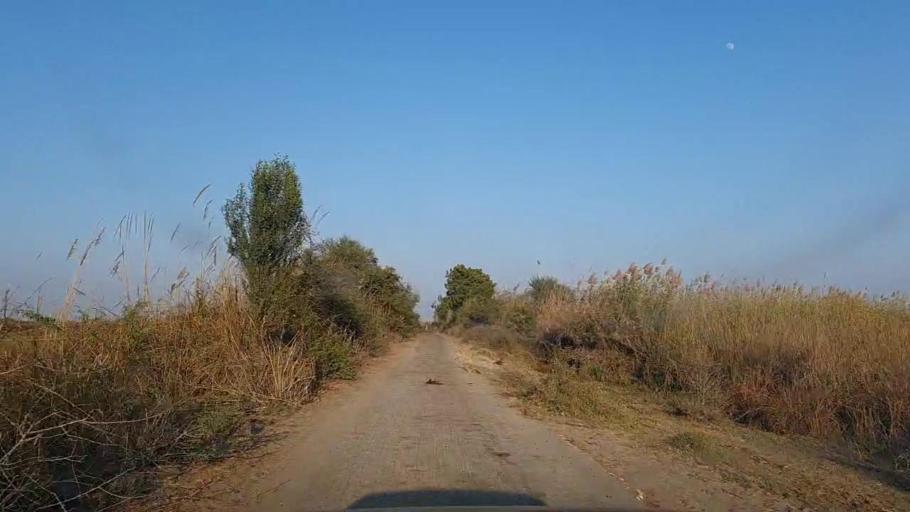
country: PK
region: Sindh
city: Sanghar
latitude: 26.2965
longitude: 68.9866
